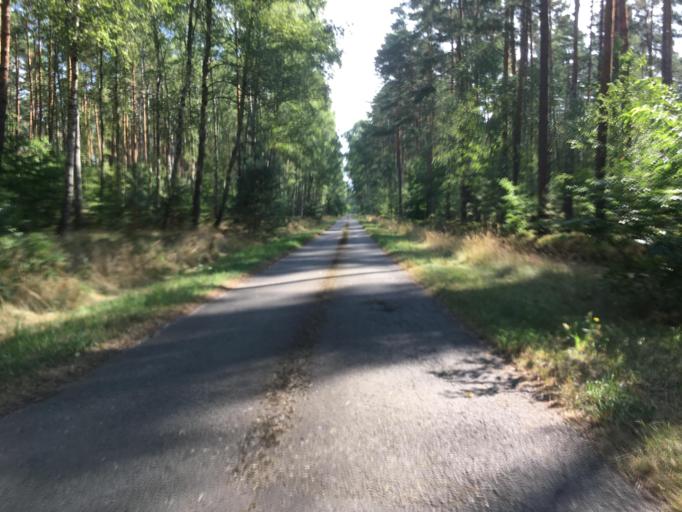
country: DE
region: Brandenburg
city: Liebenwalde
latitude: 52.9285
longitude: 13.4660
